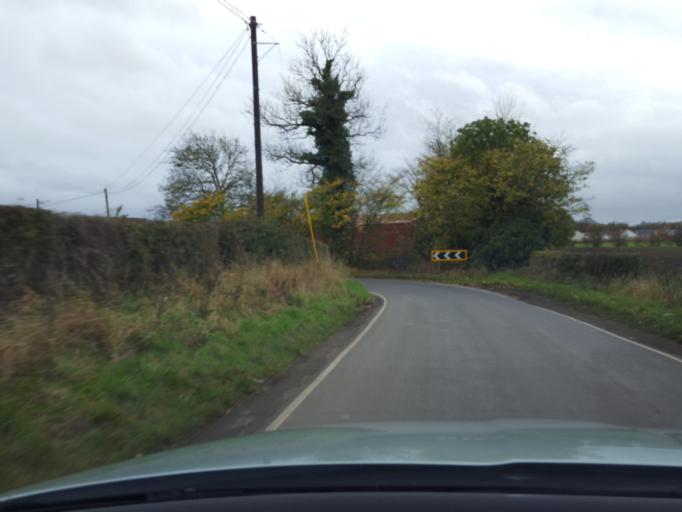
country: GB
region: Scotland
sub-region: West Lothian
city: East Calder
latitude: 55.9025
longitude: -3.4452
